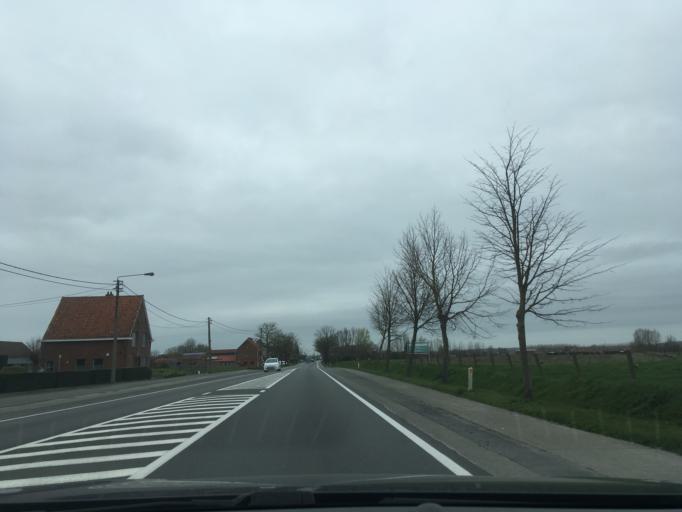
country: BE
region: Flanders
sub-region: Provincie West-Vlaanderen
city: Torhout
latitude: 51.0243
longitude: 3.1040
